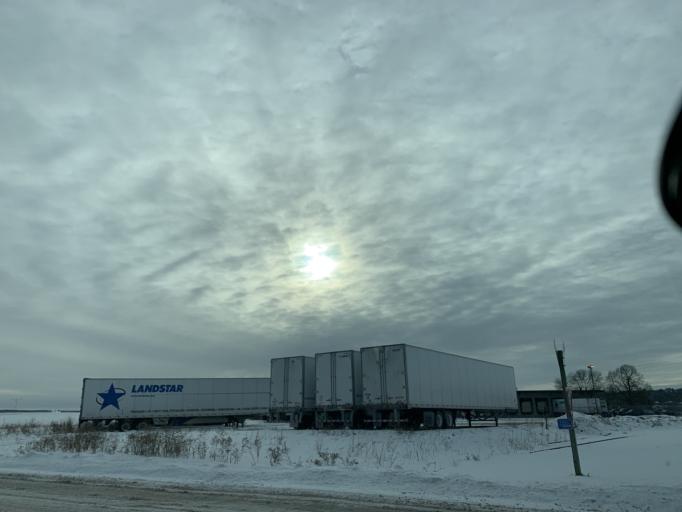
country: US
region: Minnesota
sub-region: Ramsey County
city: Saint Paul
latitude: 44.9444
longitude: -93.0721
